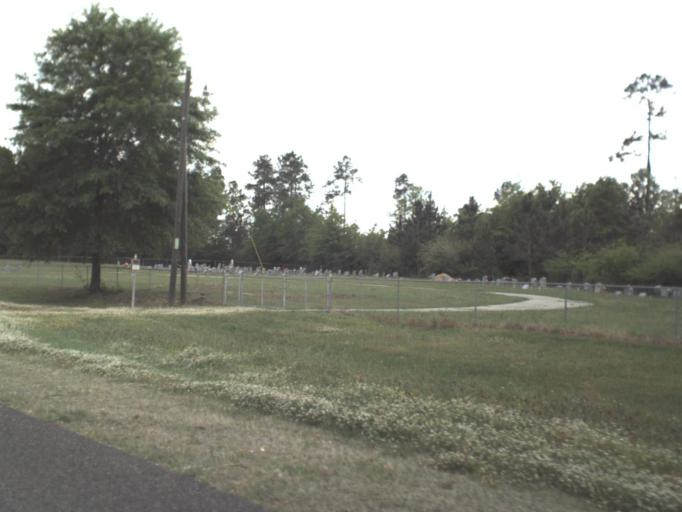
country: US
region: Florida
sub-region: Escambia County
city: Cantonment
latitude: 30.6505
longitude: -87.3515
